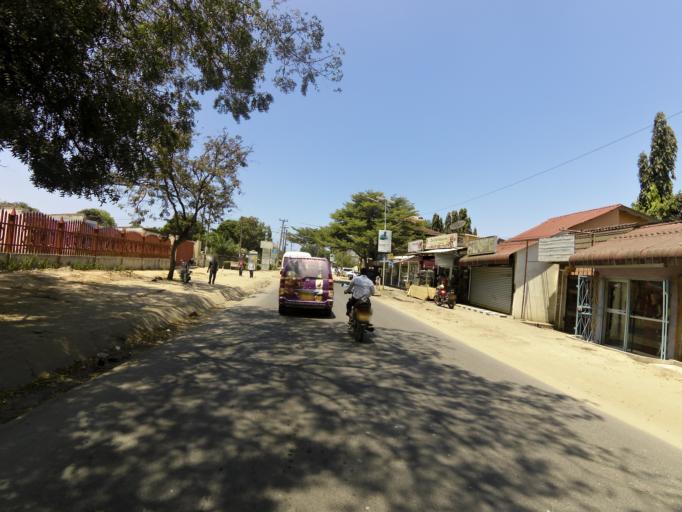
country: TZ
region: Dar es Salaam
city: Magomeni
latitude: -6.7902
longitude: 39.2692
